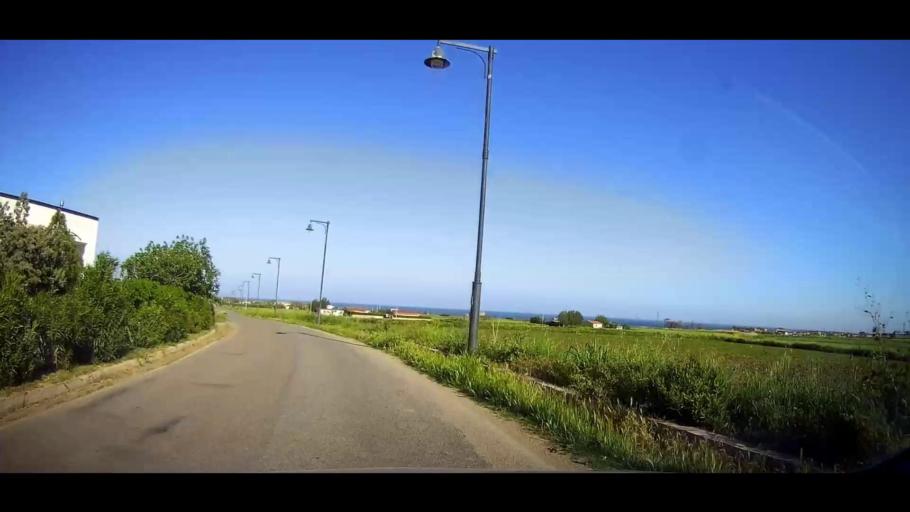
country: IT
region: Calabria
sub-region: Provincia di Crotone
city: Crotone
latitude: 39.0247
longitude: 17.1707
